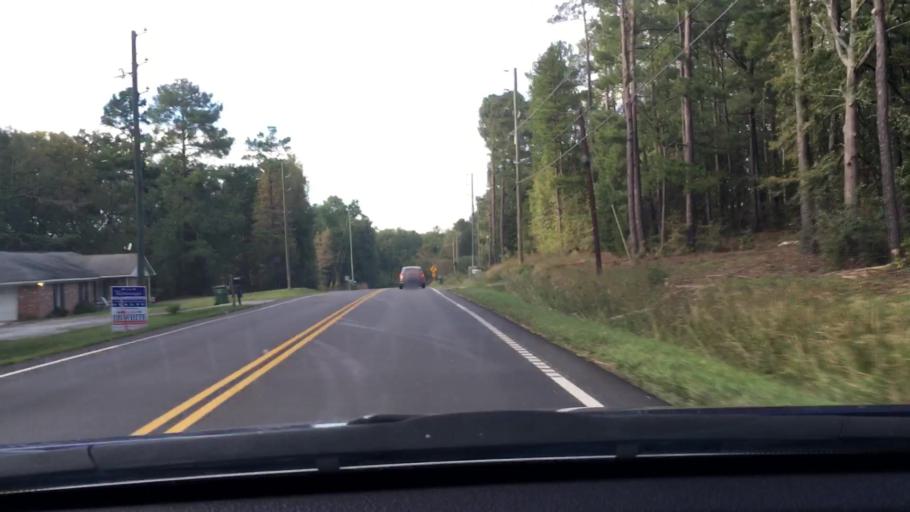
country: US
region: South Carolina
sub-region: Lexington County
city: Irmo
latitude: 34.1059
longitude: -81.1610
